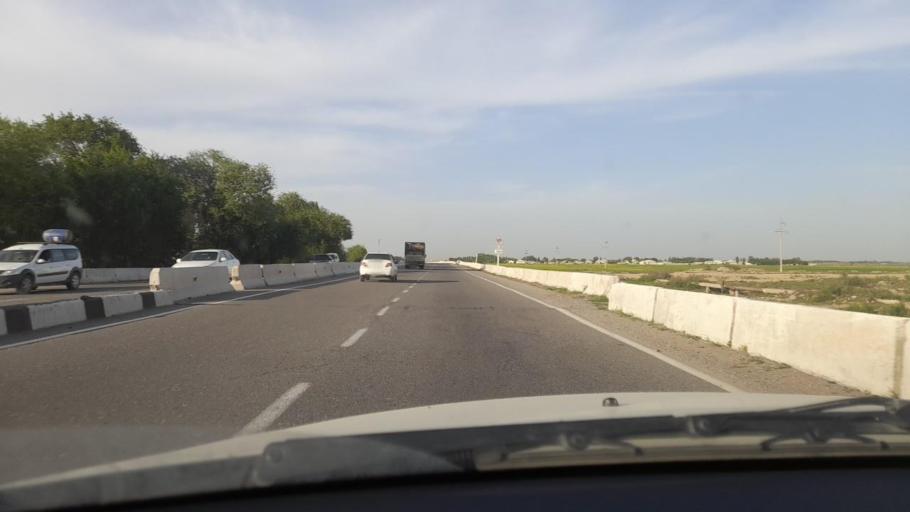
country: UZ
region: Jizzax
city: Paxtakor
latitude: 40.3170
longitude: 68.0910
